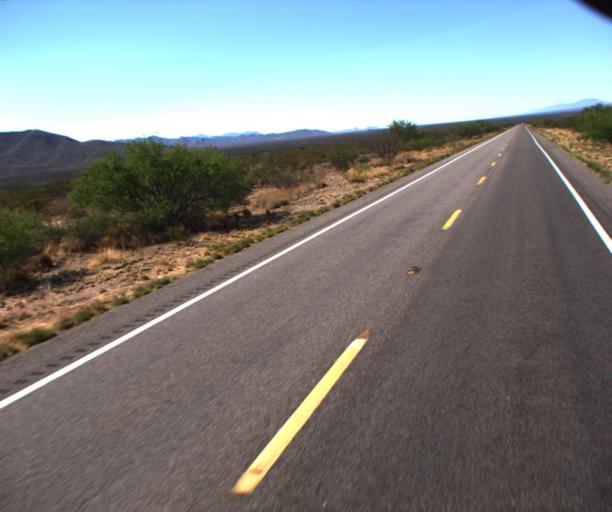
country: US
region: Arizona
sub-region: Cochise County
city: Tombstone
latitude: 31.6276
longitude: -110.0480
